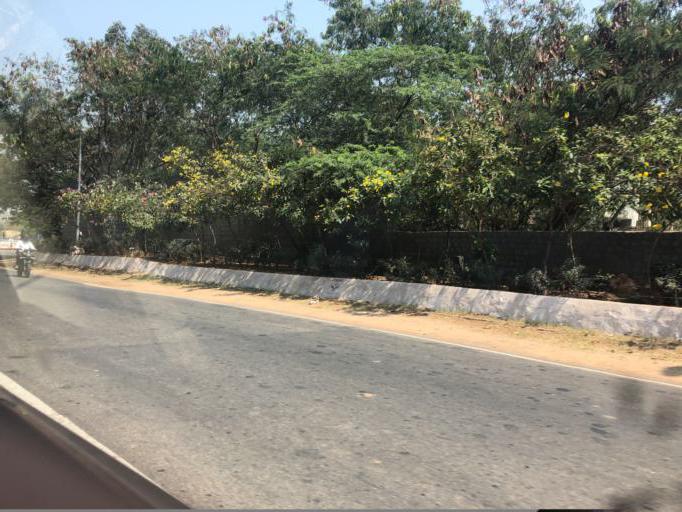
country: IN
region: Andhra Pradesh
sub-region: Vishakhapatnam
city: Yarada
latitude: 17.6971
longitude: 83.2681
